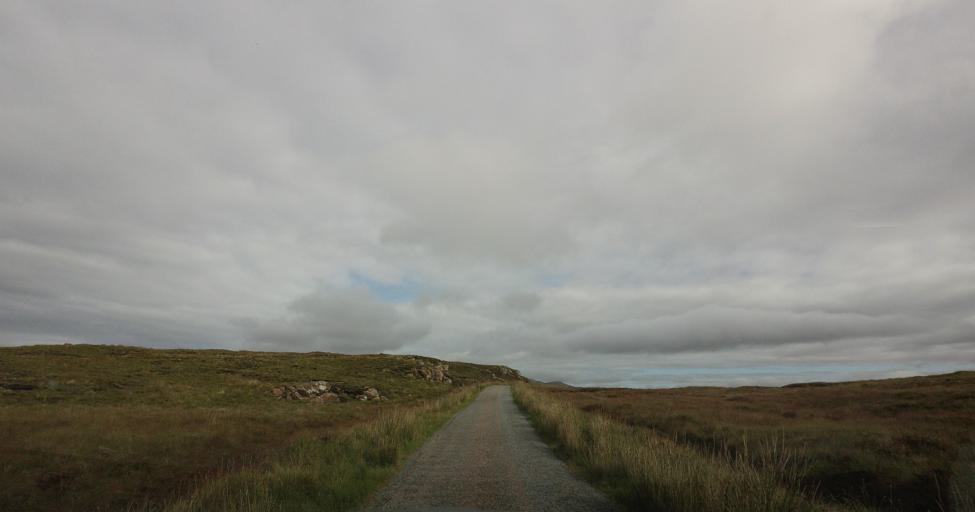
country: GB
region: Scotland
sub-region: Highland
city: Isle of Skye
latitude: 57.4104
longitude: -6.2639
